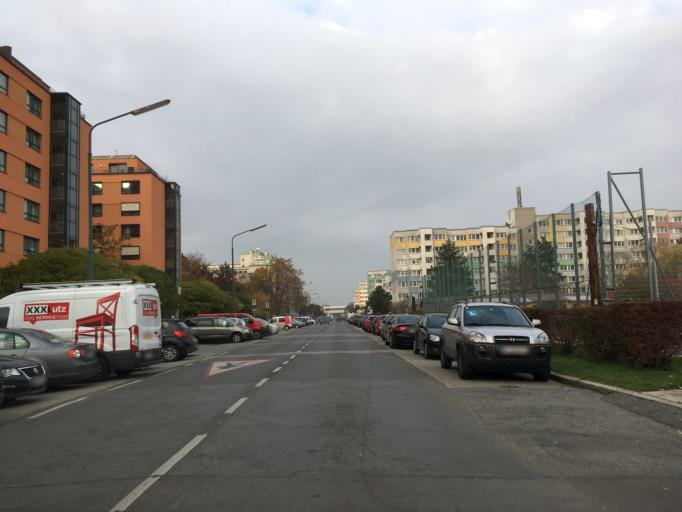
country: AT
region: Lower Austria
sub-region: Politischer Bezirk Wien-Umgebung
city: Gerasdorf bei Wien
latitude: 48.2549
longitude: 16.4565
